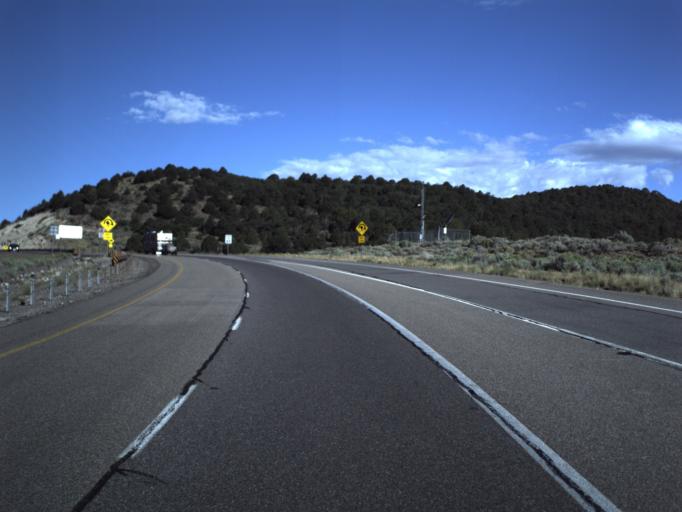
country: US
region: Utah
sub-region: Beaver County
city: Beaver
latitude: 38.5904
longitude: -112.4928
